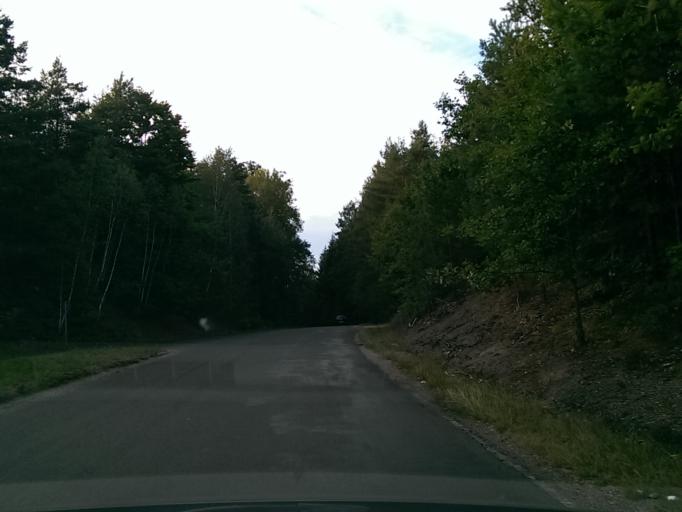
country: CZ
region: Central Bohemia
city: Dolni Bousov
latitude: 50.4981
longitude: 15.1219
